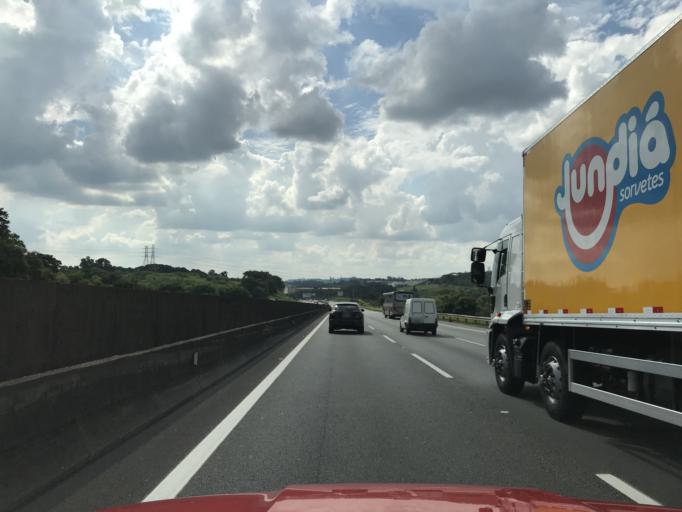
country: BR
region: Sao Paulo
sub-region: Louveira
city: Louveira
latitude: -23.1213
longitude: -46.9545
